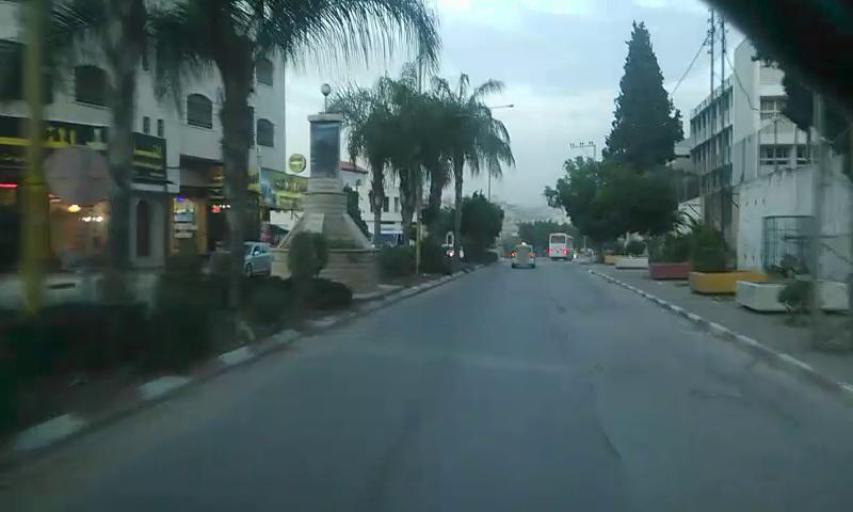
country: PS
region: West Bank
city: Dhannabah
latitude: 32.3174
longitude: 35.0341
